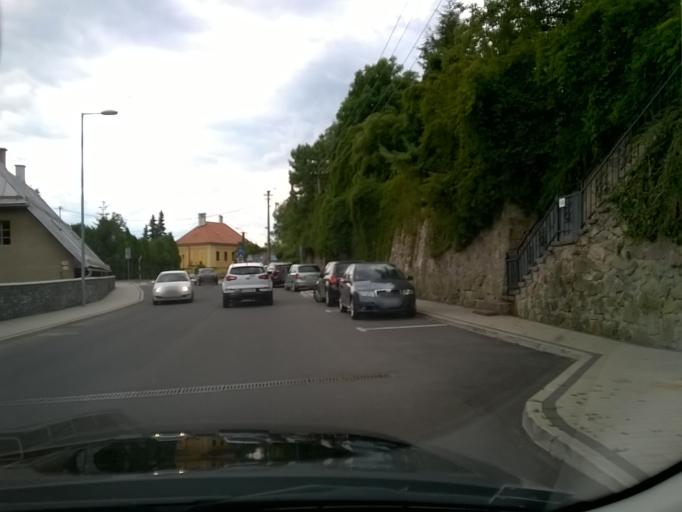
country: SK
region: Banskobystricky
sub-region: Okres Banska Bystrica
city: Banska Stiavnica
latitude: 48.4617
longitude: 18.9010
